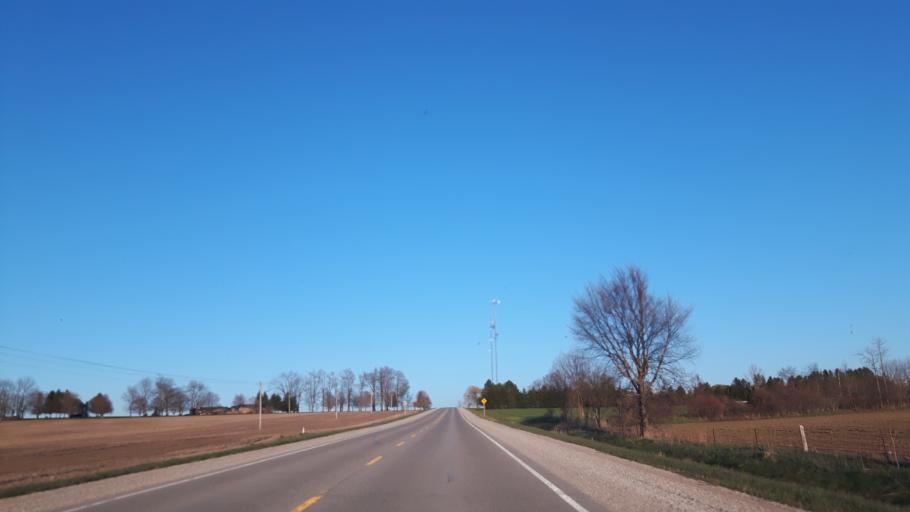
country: CA
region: Ontario
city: Bluewater
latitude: 43.5237
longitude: -81.5565
